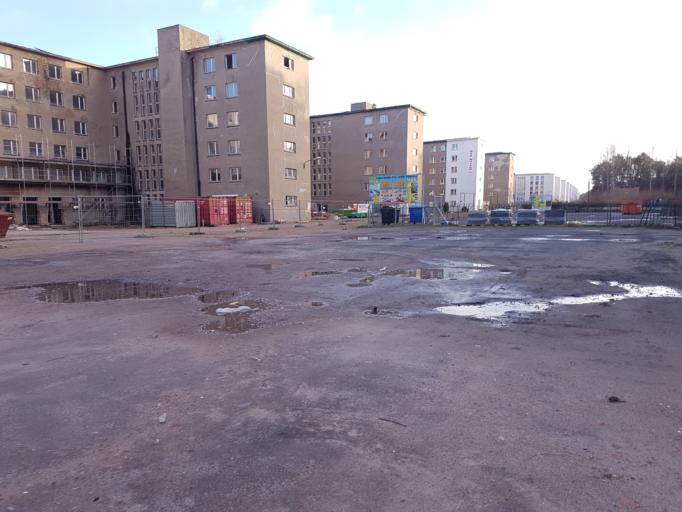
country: DE
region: Mecklenburg-Vorpommern
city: Ostseebad Binz
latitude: 54.4368
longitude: 13.5760
